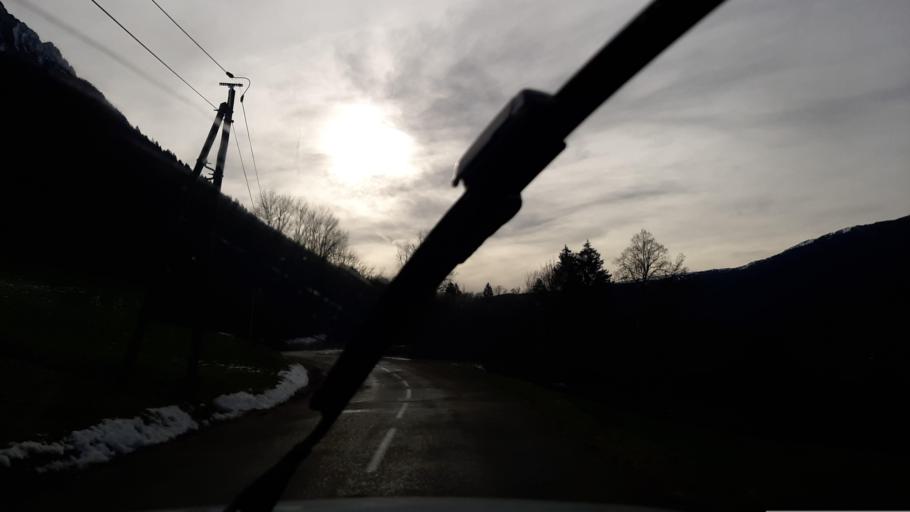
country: FR
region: Rhone-Alpes
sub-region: Departement de la Haute-Savoie
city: Cusy
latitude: 45.6774
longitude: 6.1120
